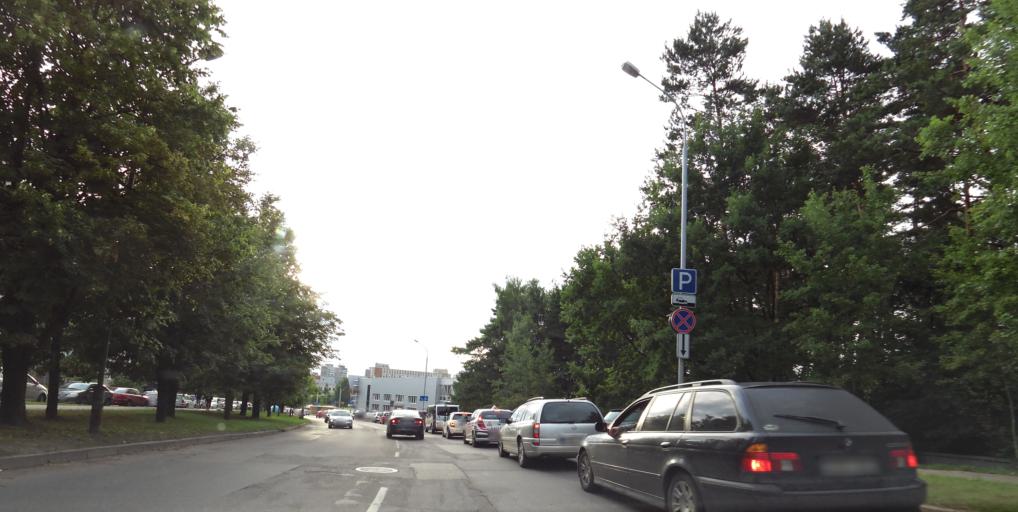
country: LT
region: Vilnius County
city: Justiniskes
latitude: 54.7069
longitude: 25.2295
